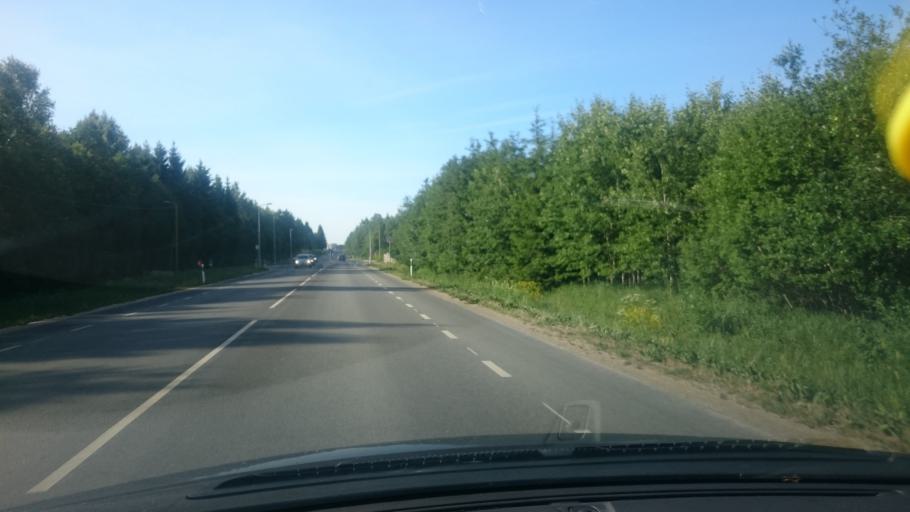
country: EE
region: Harju
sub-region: Saku vald
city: Saku
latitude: 59.2800
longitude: 24.6653
